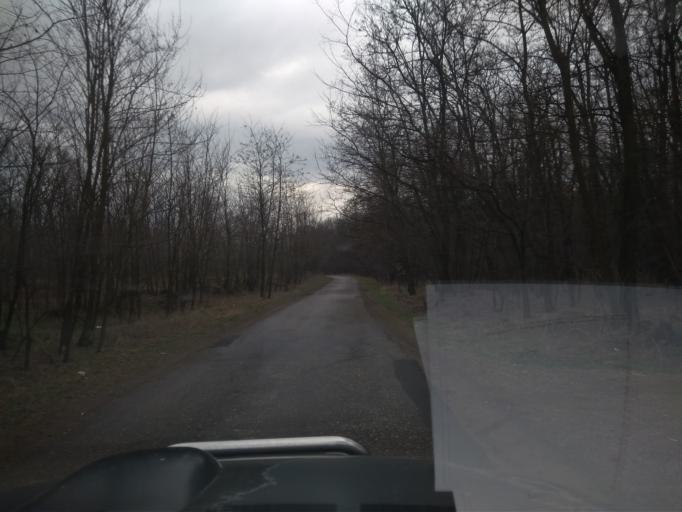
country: HU
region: Szabolcs-Szatmar-Bereg
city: Nyirpazony
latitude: 48.0184
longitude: 21.8078
